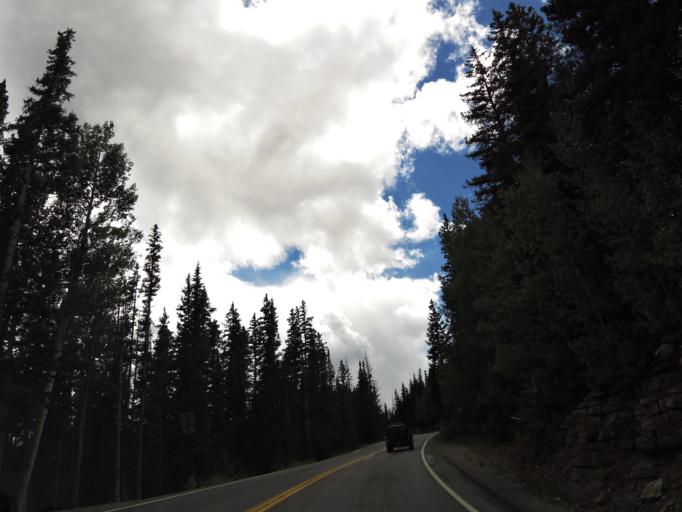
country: US
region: Colorado
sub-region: San Juan County
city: Silverton
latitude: 37.7696
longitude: -107.6713
